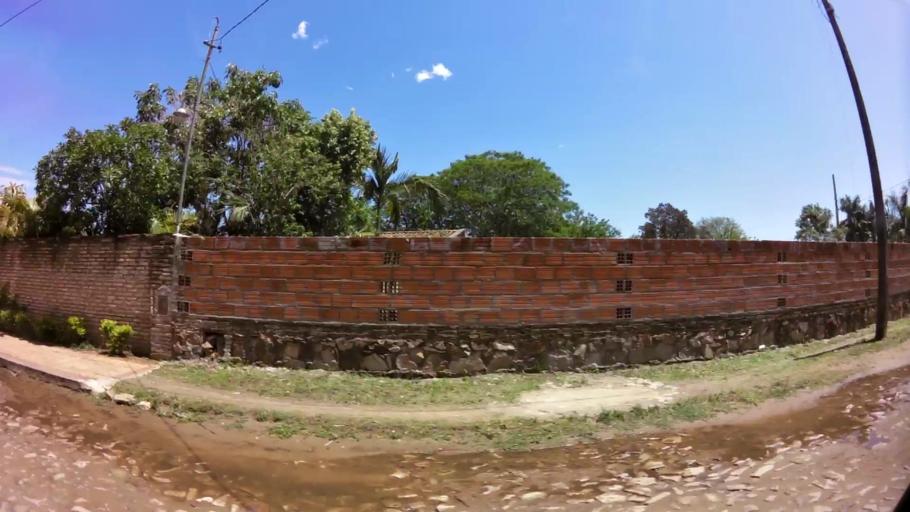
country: PY
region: Central
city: Colonia Mariano Roque Alonso
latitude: -25.1939
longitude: -57.5483
